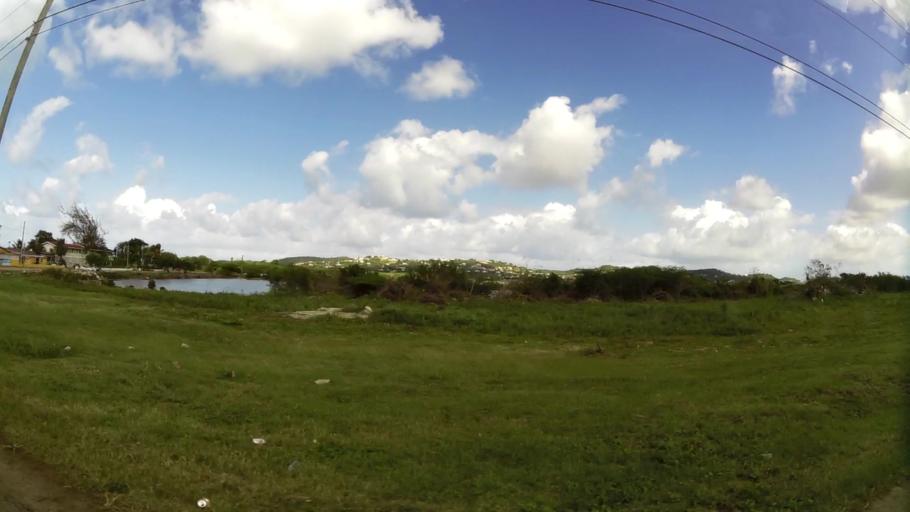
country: AG
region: Saint John
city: Saint John's
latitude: 17.1414
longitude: -61.8583
